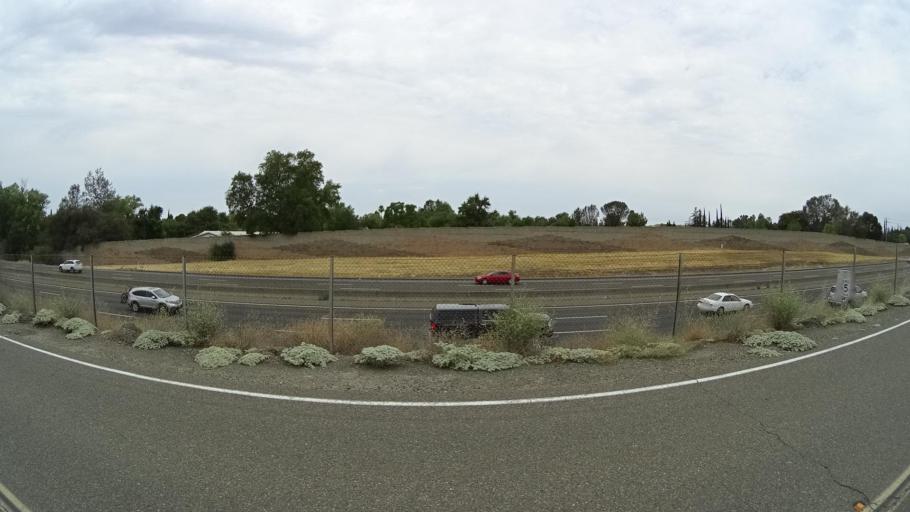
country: US
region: California
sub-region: Placer County
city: Rocklin
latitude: 38.7827
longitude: -121.2289
